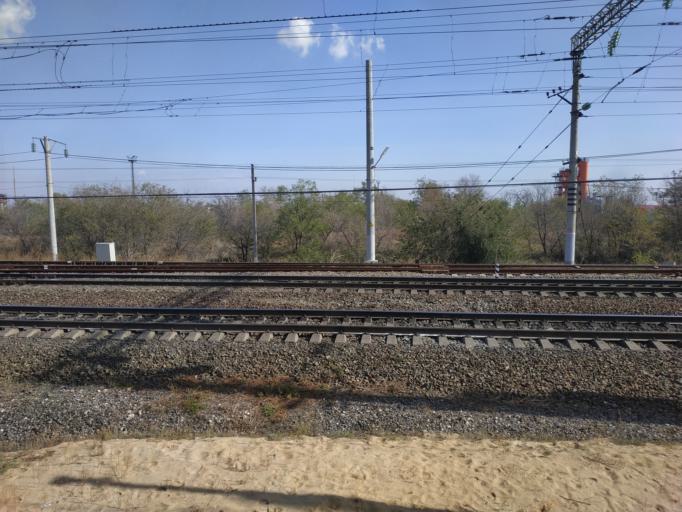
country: RU
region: Volgograd
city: Gumrak
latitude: 48.7925
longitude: 44.3657
